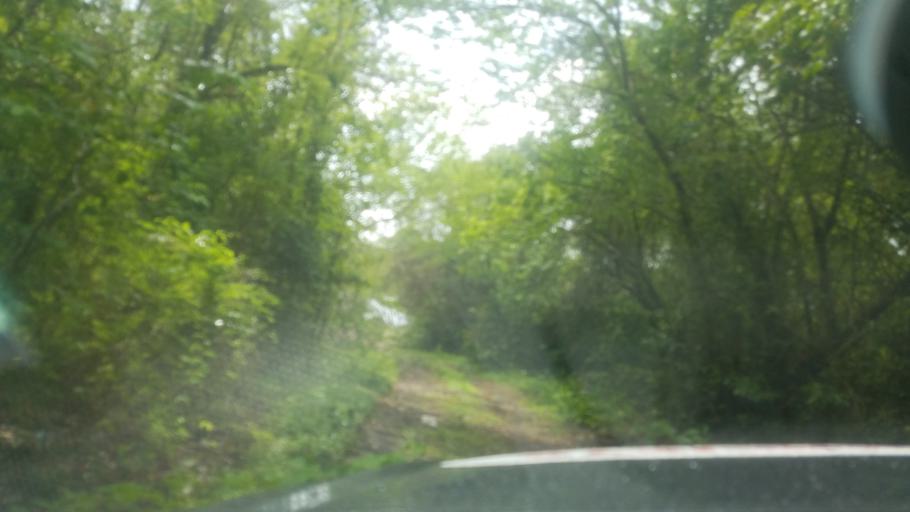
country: LC
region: Laborie Quarter
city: Laborie
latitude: 13.7344
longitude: -60.9786
